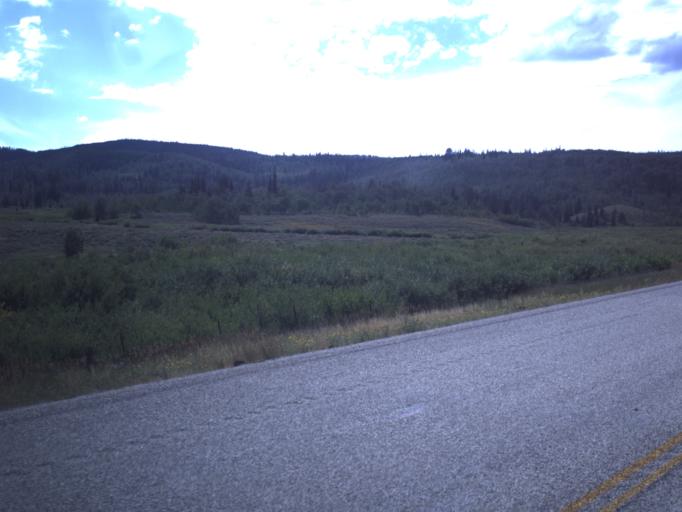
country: US
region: Utah
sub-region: Wasatch County
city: Heber
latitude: 40.2884
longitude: -111.2453
